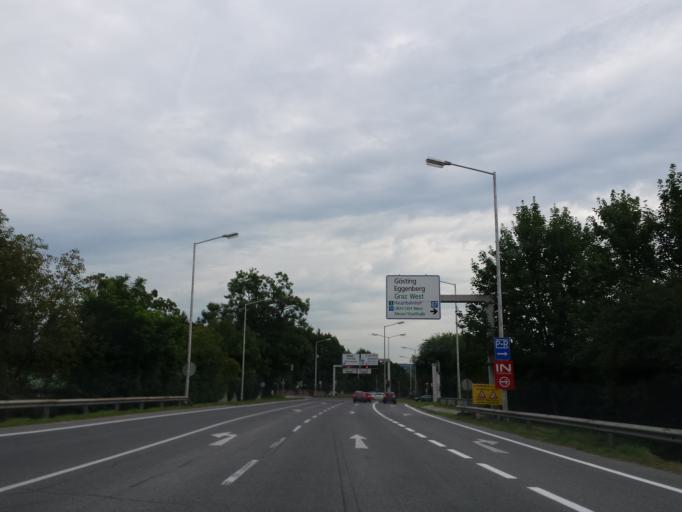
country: AT
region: Styria
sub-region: Graz Stadt
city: Goesting
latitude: 47.1098
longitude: 15.4013
